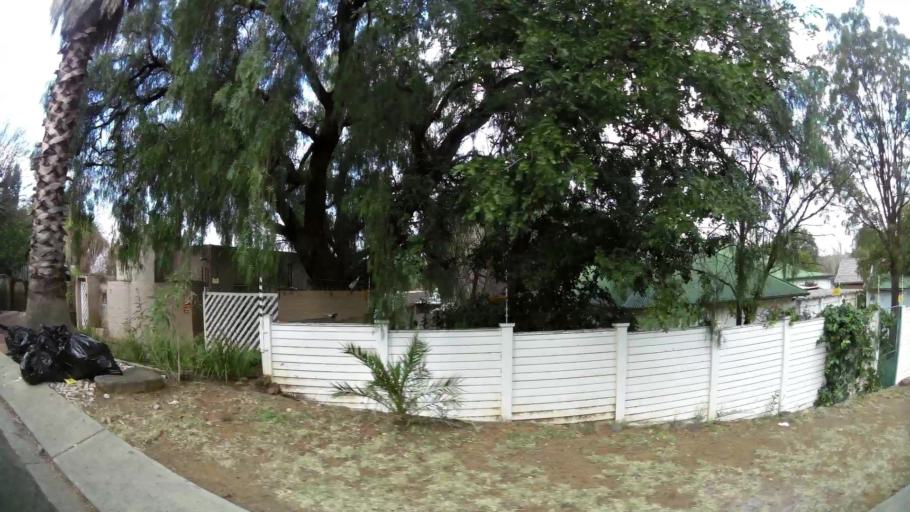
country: ZA
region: Orange Free State
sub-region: Mangaung Metropolitan Municipality
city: Bloemfontein
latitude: -29.0842
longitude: 26.2046
